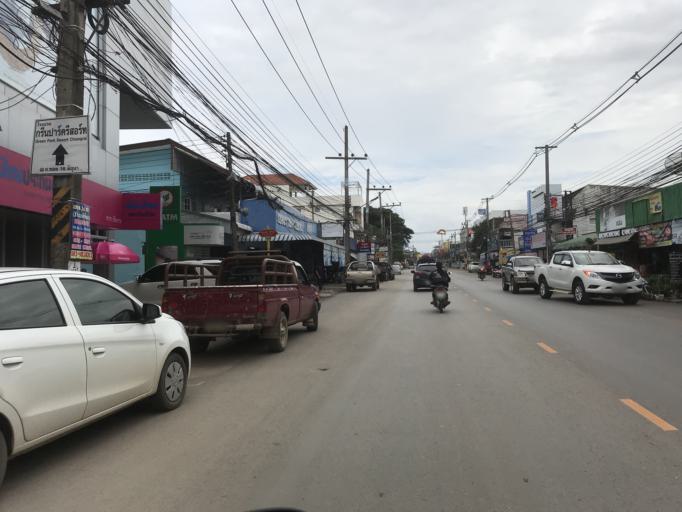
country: TH
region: Chiang Rai
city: Chiang Rai
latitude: 19.8950
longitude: 99.8315
